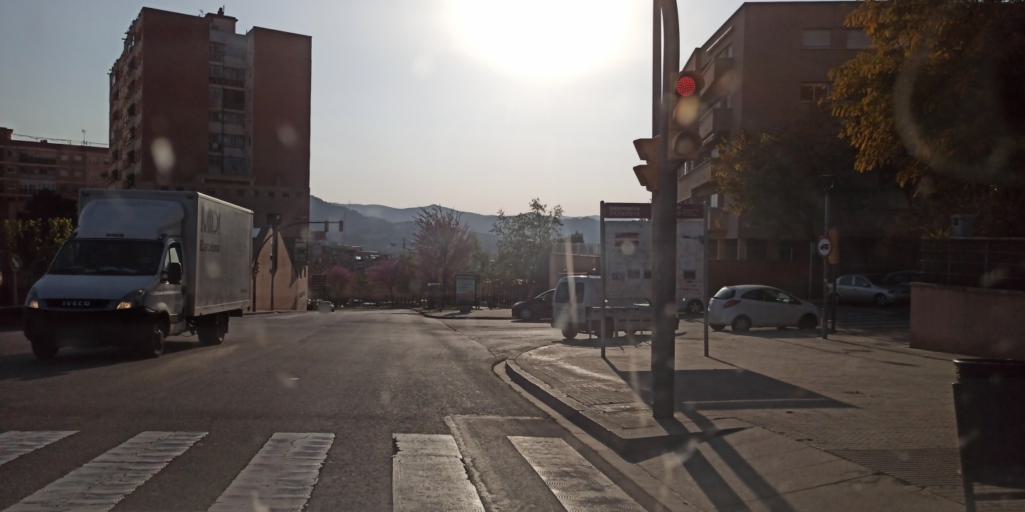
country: ES
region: Catalonia
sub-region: Provincia de Barcelona
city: Sant Feliu de Llobregat
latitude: 41.3892
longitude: 2.0467
